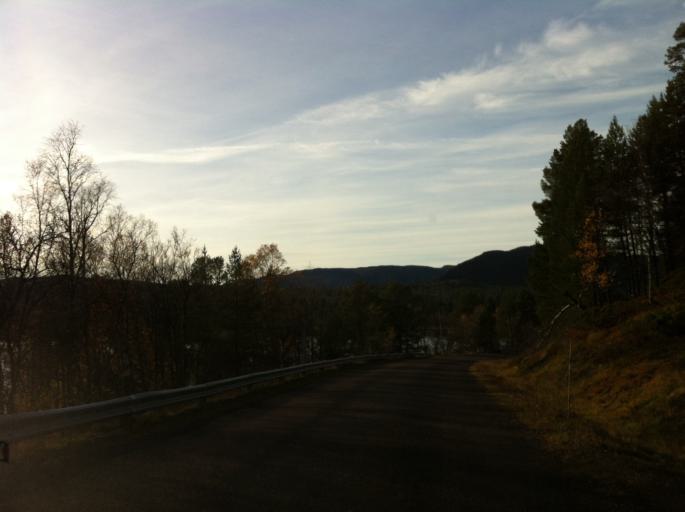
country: NO
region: Hedmark
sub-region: Engerdal
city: Engerdal
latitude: 62.0835
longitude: 12.1055
